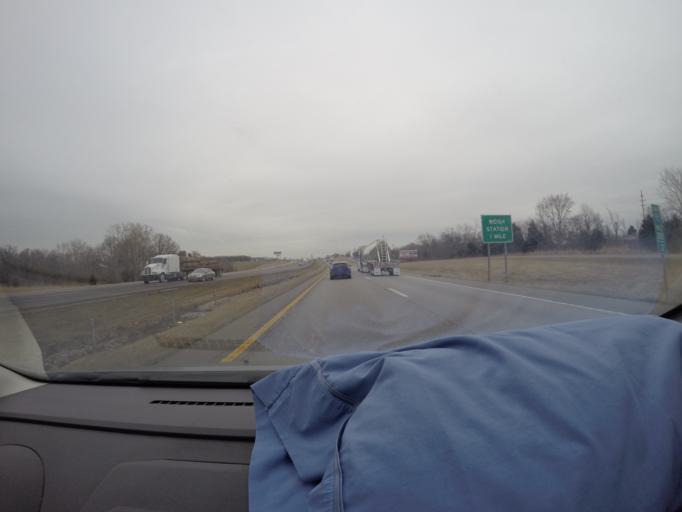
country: US
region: Missouri
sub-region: Warren County
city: Wright City
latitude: 38.8181
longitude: -90.9665
